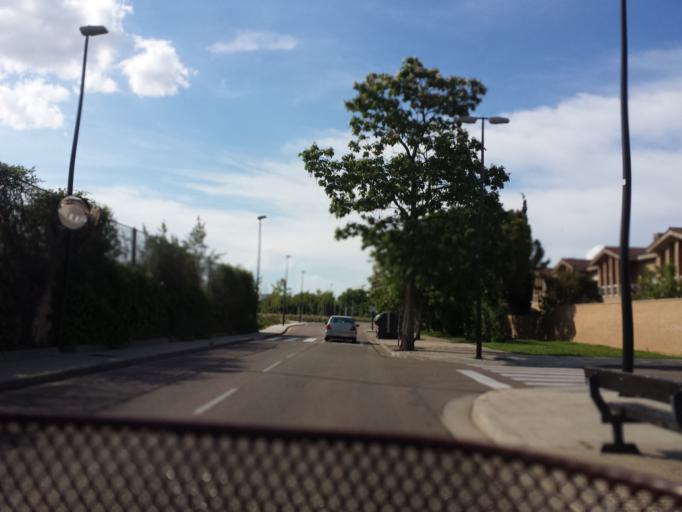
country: ES
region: Aragon
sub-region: Provincia de Zaragoza
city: Oliver-Valdefierro, Oliver, Valdefierro
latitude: 41.6333
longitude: -0.9215
